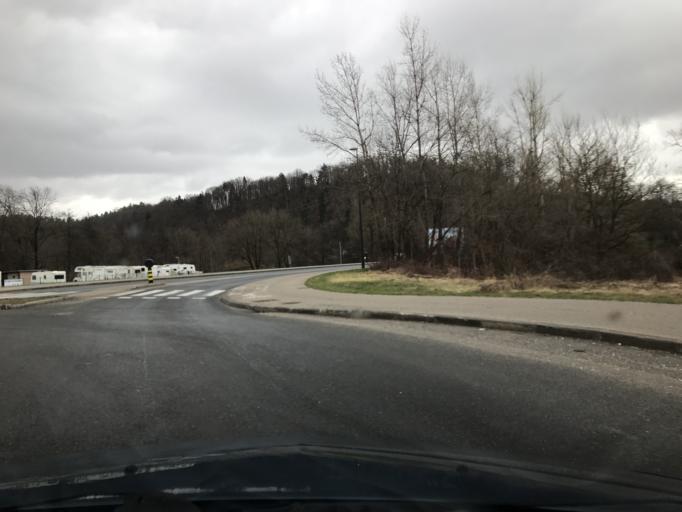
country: SI
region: Ljubljana
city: Ljubljana
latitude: 46.0993
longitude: 14.5170
